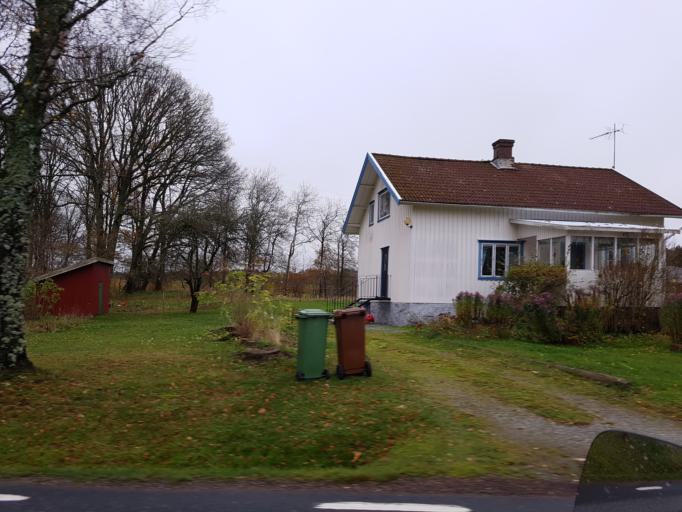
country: SE
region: Vaestra Goetaland
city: Svanesund
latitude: 58.1549
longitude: 11.7950
